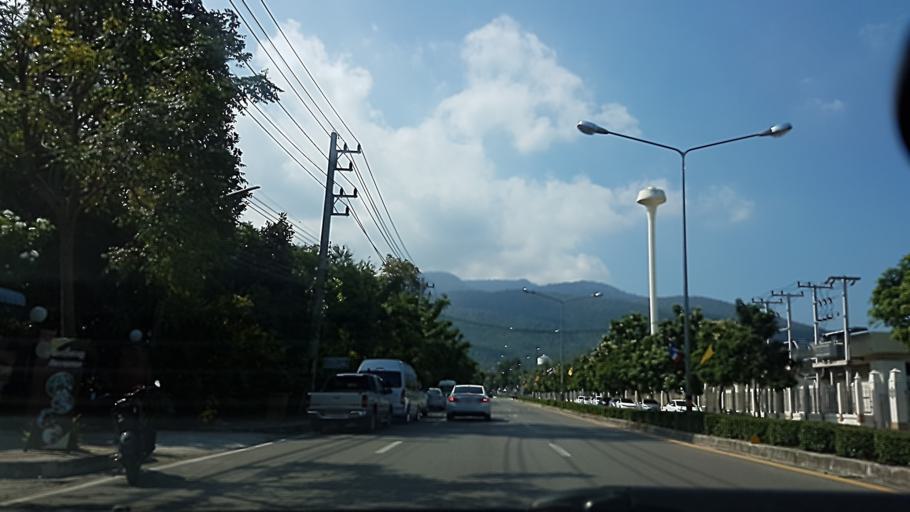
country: TH
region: Chiang Mai
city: Chiang Mai
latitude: 18.8244
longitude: 98.9611
